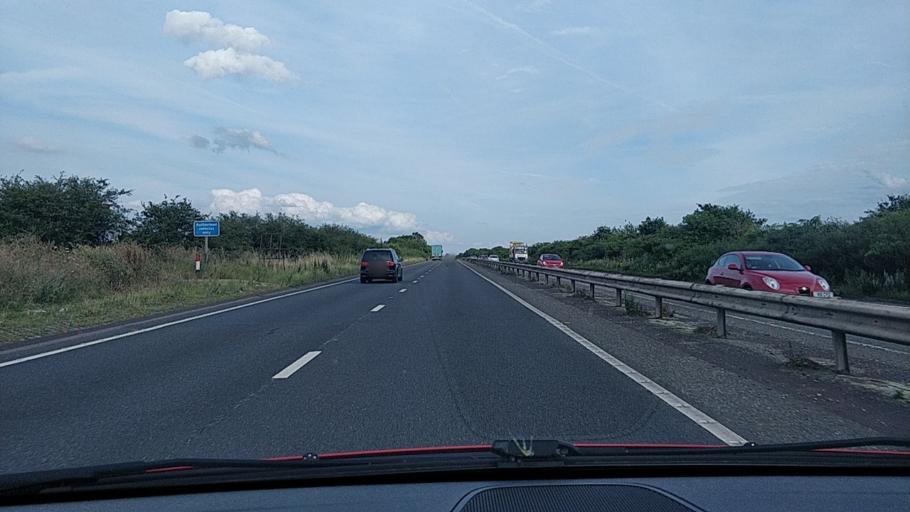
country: GB
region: Wales
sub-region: Wrexham
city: Rossett
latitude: 53.1580
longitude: -2.9370
